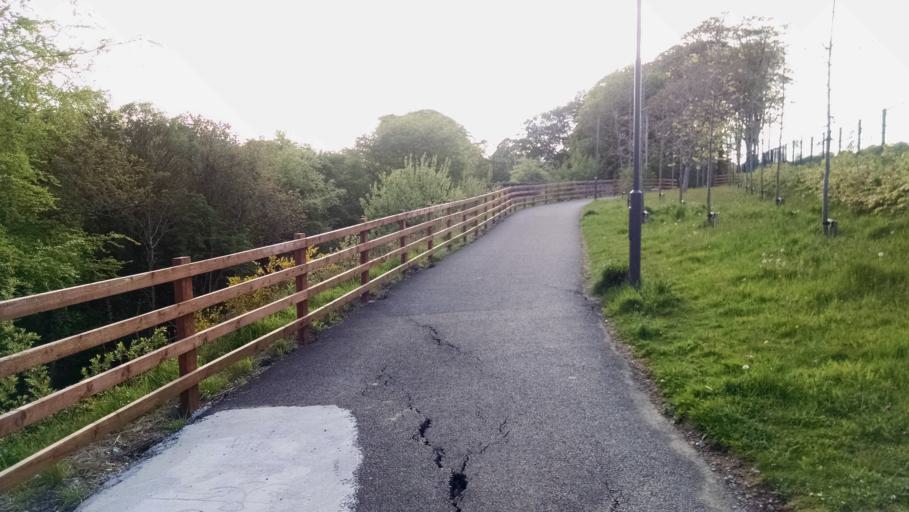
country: IE
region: Connaught
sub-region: Maigh Eo
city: Westport
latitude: 53.7997
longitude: -9.5112
